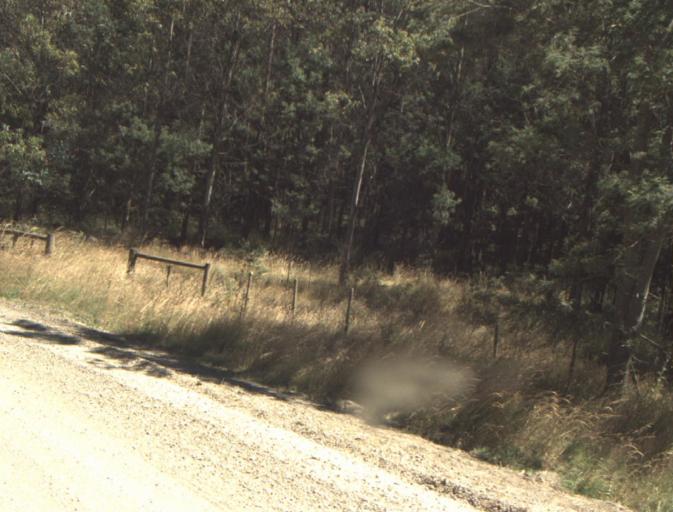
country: AU
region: Tasmania
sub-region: Dorset
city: Scottsdale
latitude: -41.3287
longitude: 147.4426
